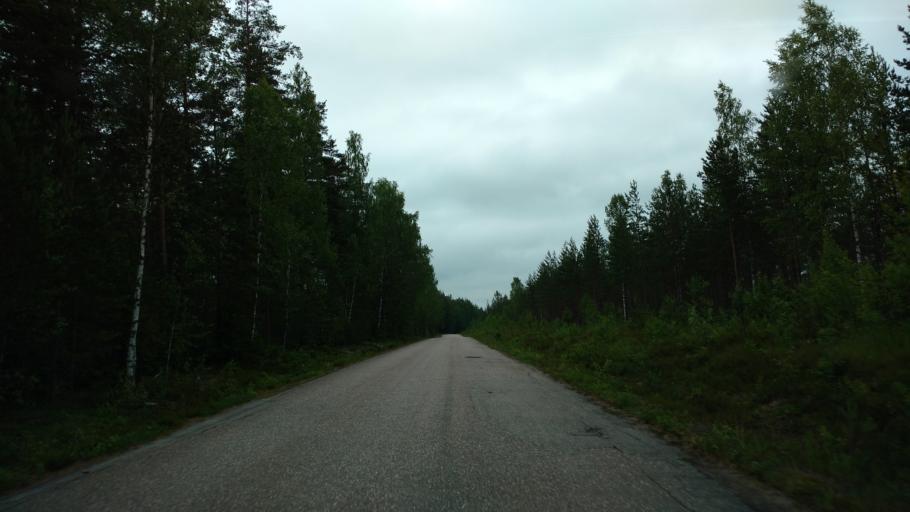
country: FI
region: Varsinais-Suomi
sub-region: Salo
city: Kiikala
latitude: 60.4546
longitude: 23.6351
